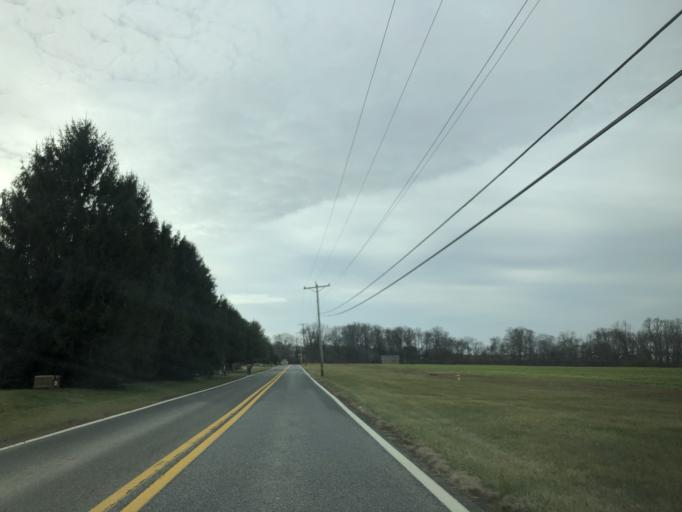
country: US
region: Delaware
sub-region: New Castle County
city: Middletown
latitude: 39.4970
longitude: -75.6876
